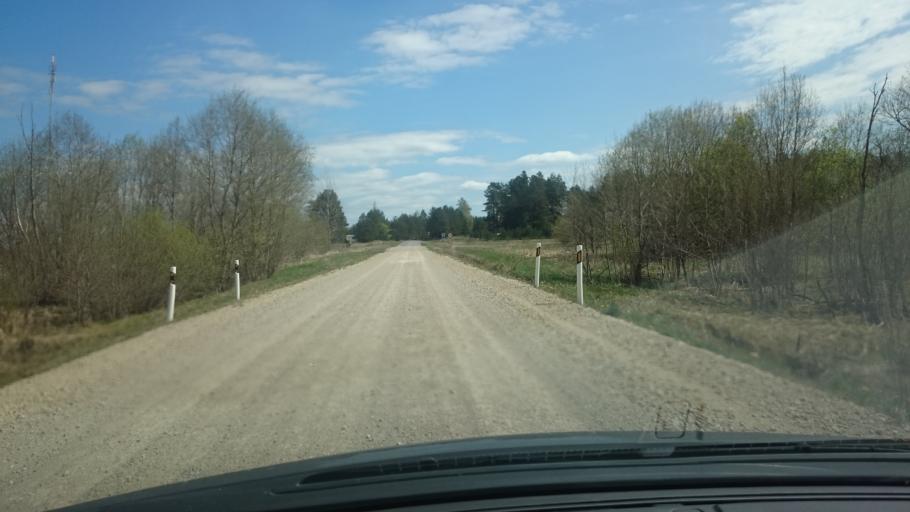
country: EE
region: Ida-Virumaa
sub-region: Sillamaee linn
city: Sillamae
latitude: 59.0848
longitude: 27.7714
